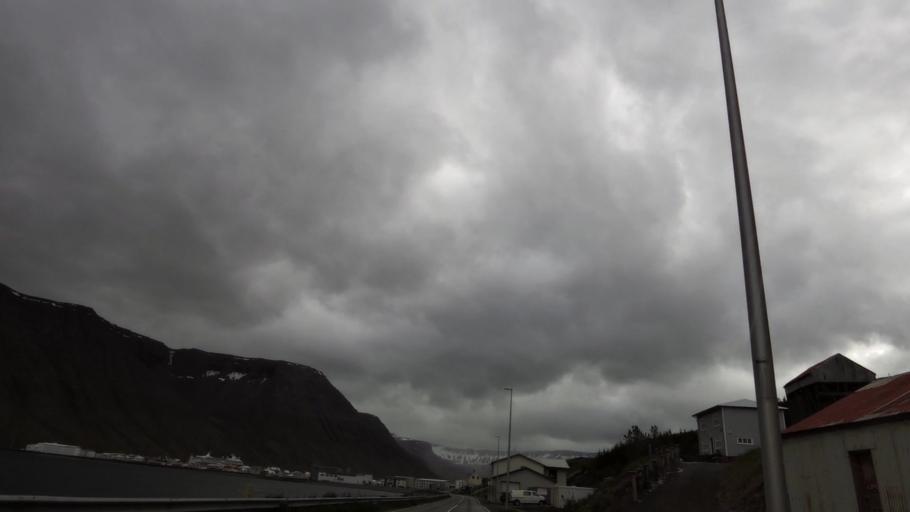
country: IS
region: Westfjords
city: Isafjoerdur
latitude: 66.0831
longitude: -23.1225
